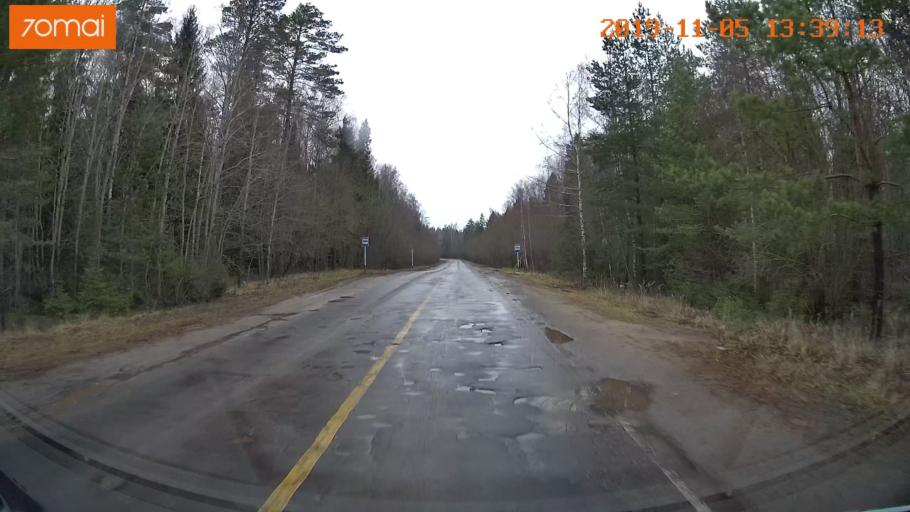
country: RU
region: Ivanovo
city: Shuya
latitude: 56.9379
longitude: 41.3869
